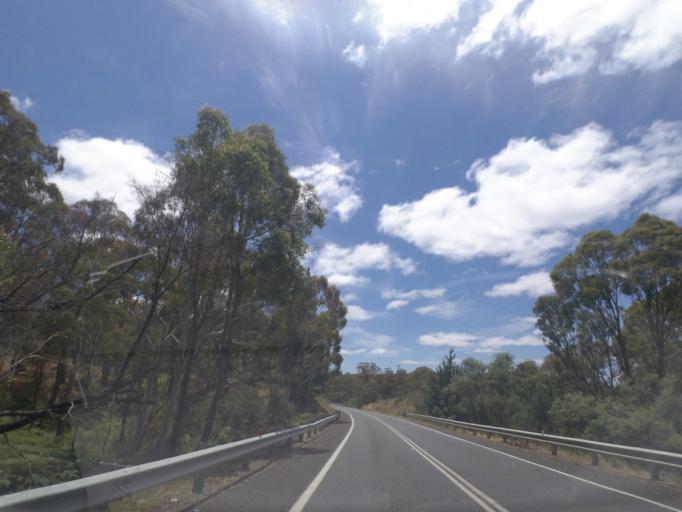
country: AU
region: Victoria
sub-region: Mount Alexander
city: Castlemaine
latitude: -37.2910
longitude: 144.1632
